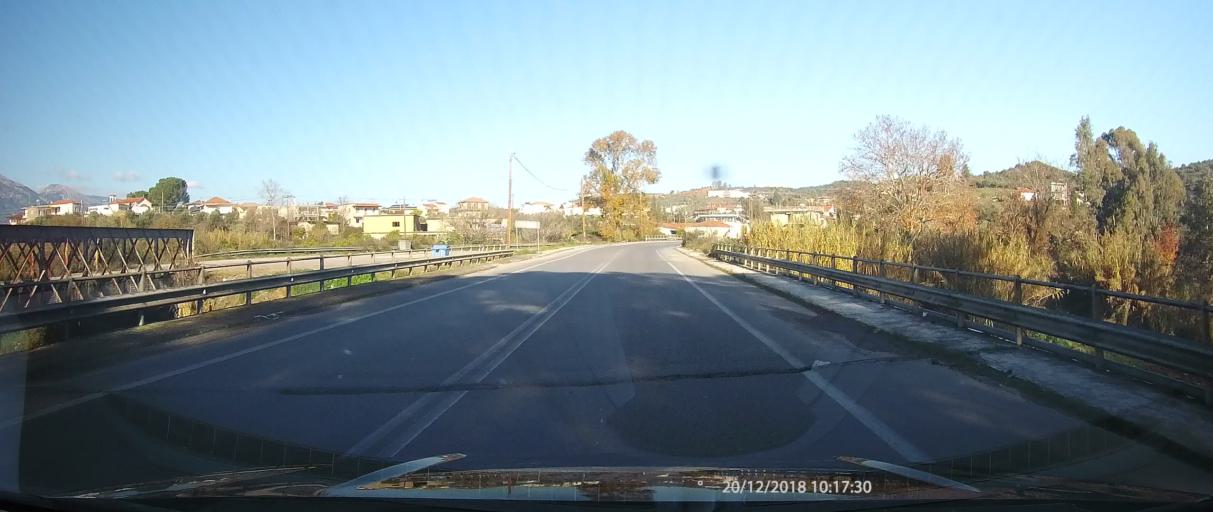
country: GR
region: Peloponnese
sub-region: Nomos Lakonias
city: Sparti
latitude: 37.1073
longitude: 22.4340
